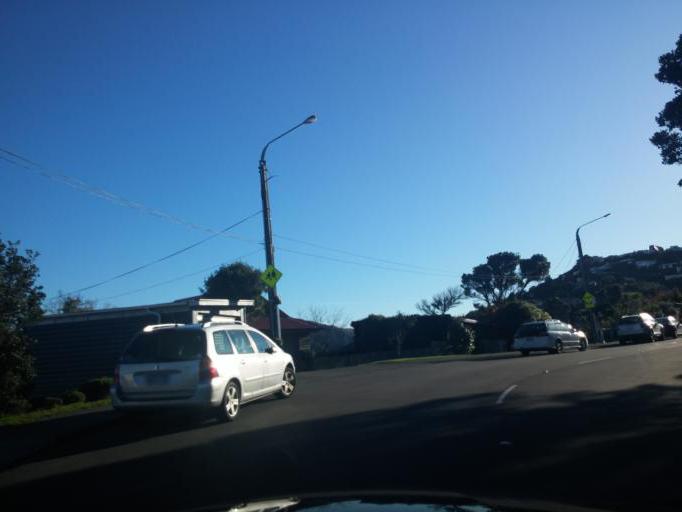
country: NZ
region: Wellington
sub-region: Wellington City
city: Kelburn
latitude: -41.2808
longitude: 174.7592
